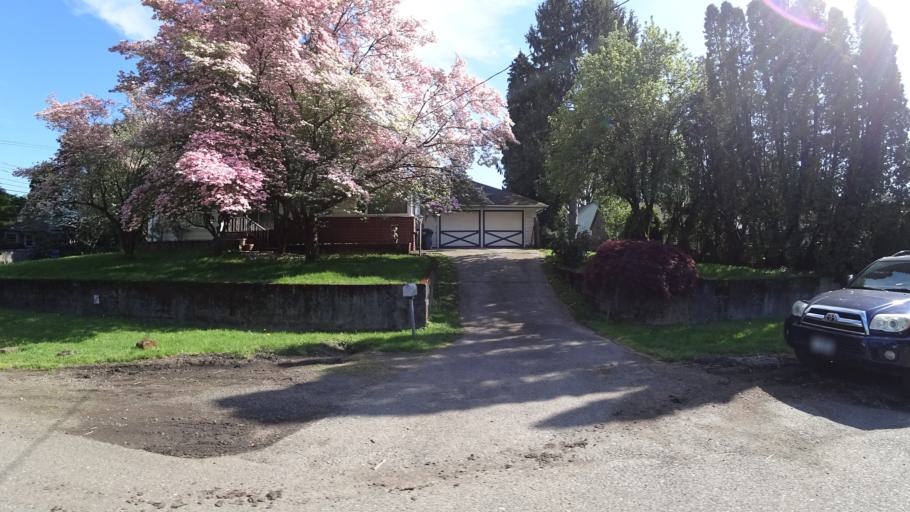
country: US
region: Oregon
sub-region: Clackamas County
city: Milwaukie
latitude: 45.4615
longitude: -122.6313
